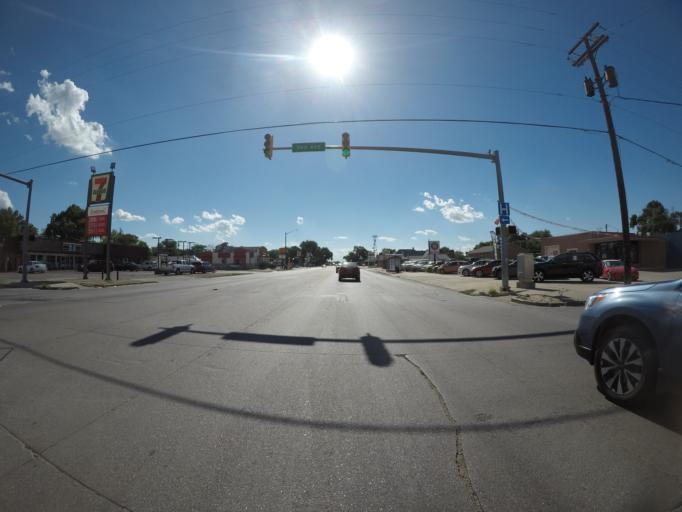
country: US
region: Colorado
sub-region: Logan County
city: Sterling
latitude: 40.6255
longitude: -103.2150
